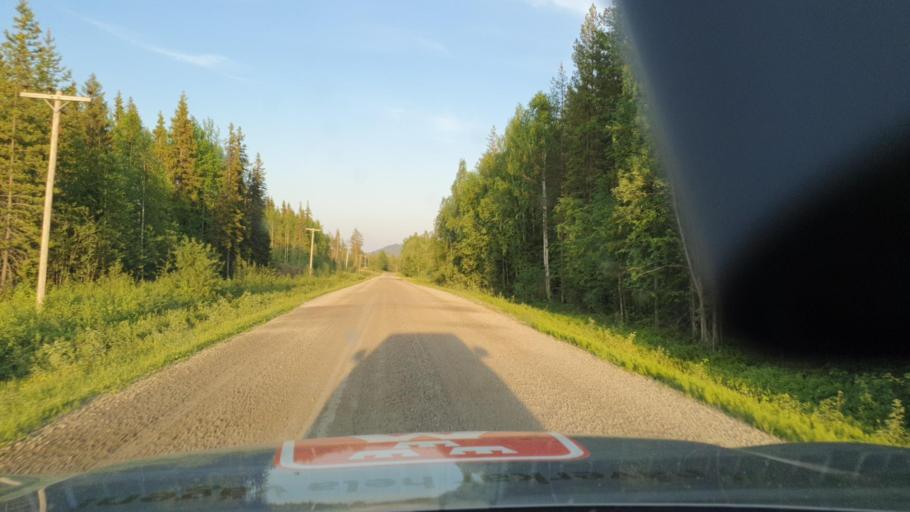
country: SE
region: Norrbotten
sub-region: Bodens Kommun
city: Boden
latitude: 66.1736
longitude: 21.5211
